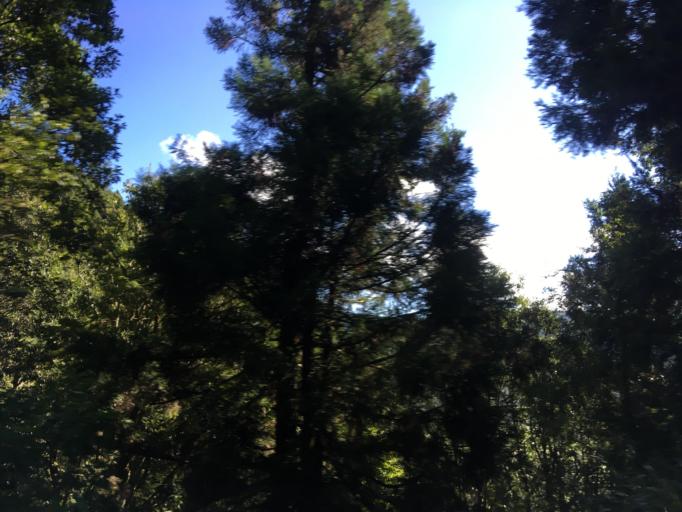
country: TW
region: Taiwan
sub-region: Yilan
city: Yilan
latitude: 24.5061
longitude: 121.5693
